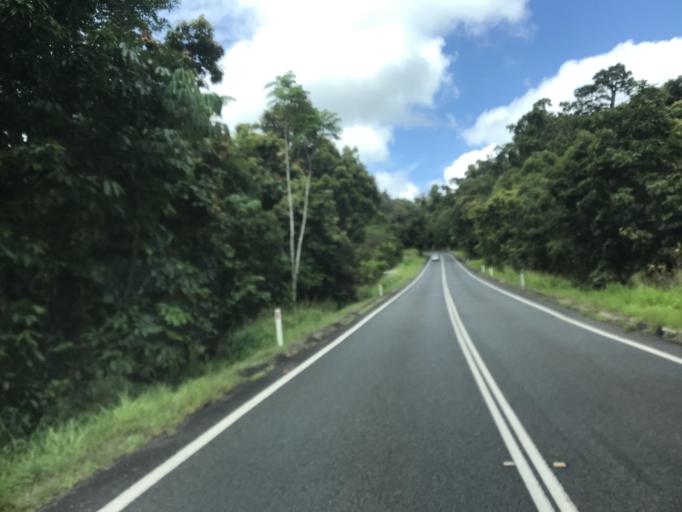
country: AU
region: Queensland
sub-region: Tablelands
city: Ravenshoe
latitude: -17.5933
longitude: 145.7340
